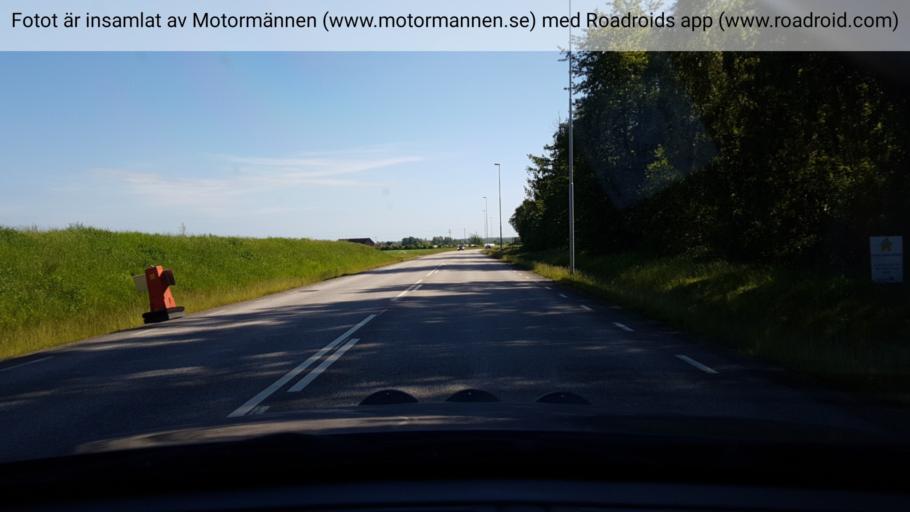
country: SE
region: Halland
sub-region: Varbergs Kommun
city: Traslovslage
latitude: 57.0954
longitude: 12.2945
